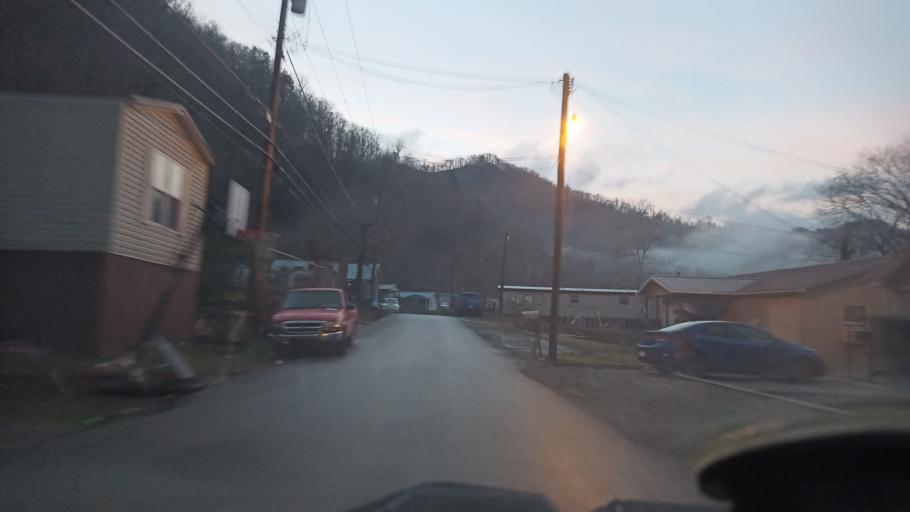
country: US
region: West Virginia
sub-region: Logan County
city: Mallory
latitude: 37.7241
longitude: -81.8755
